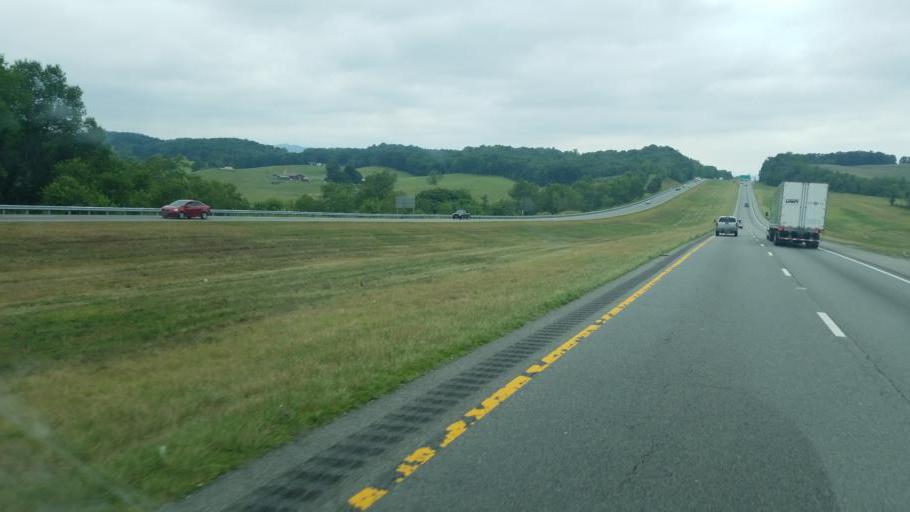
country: US
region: Virginia
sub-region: Pulaski County
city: Pulaski
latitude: 36.9093
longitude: -80.8850
